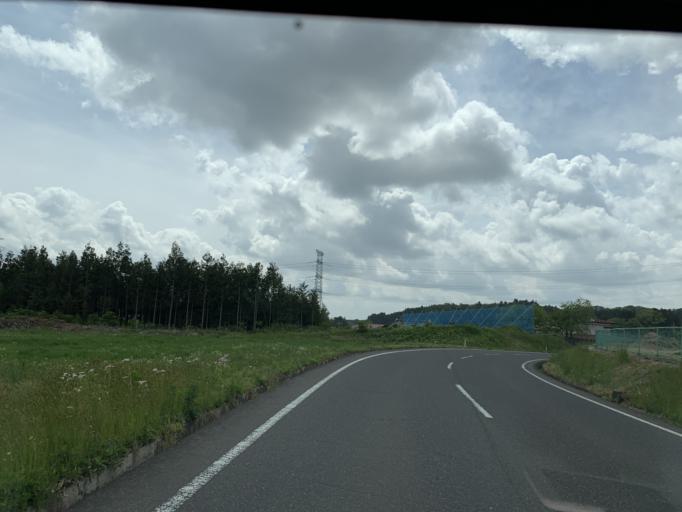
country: JP
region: Iwate
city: Ichinoseki
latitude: 38.8153
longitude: 141.0211
